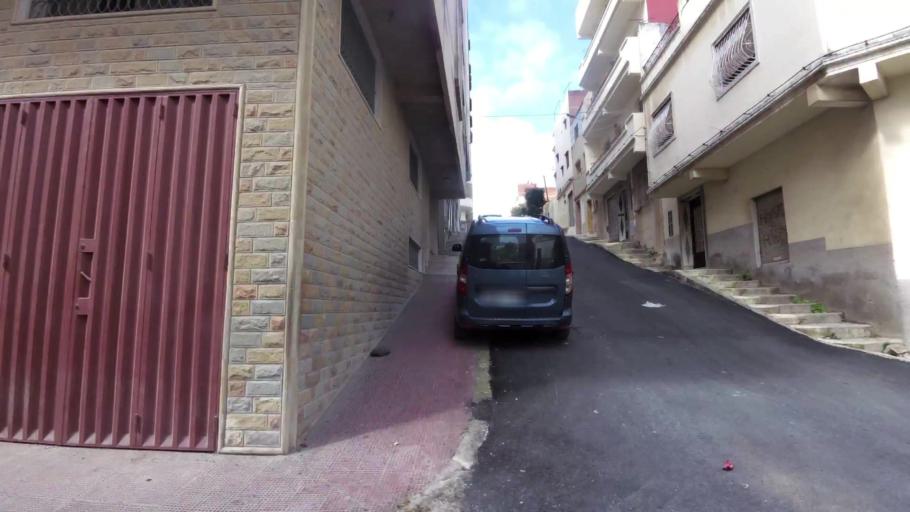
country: MA
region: Tanger-Tetouan
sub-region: Tanger-Assilah
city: Tangier
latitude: 35.7719
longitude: -5.8258
